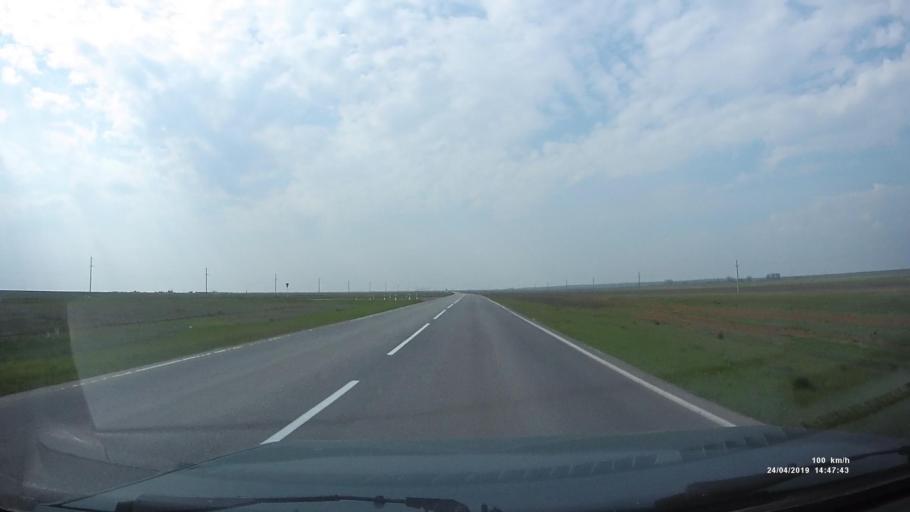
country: RU
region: Rostov
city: Remontnoye
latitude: 46.4942
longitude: 43.7682
